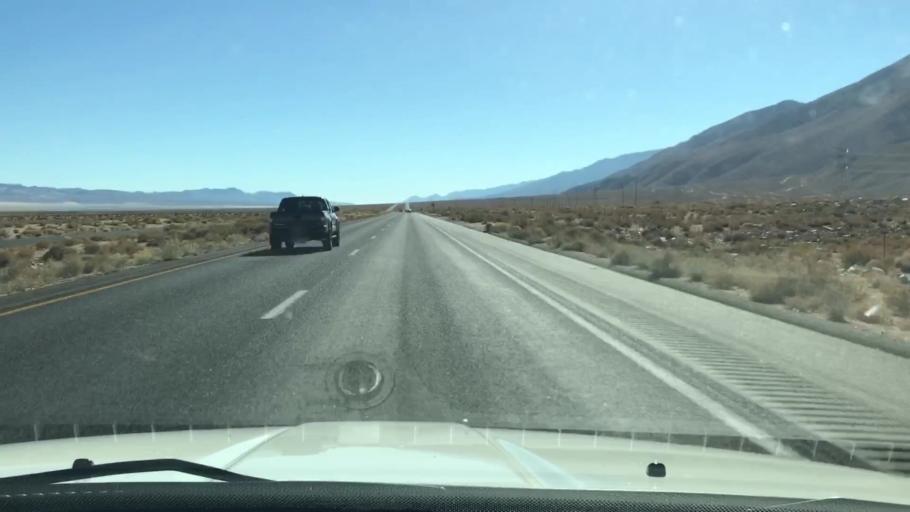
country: US
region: California
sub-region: Inyo County
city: Lone Pine
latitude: 36.4221
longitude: -118.0301
